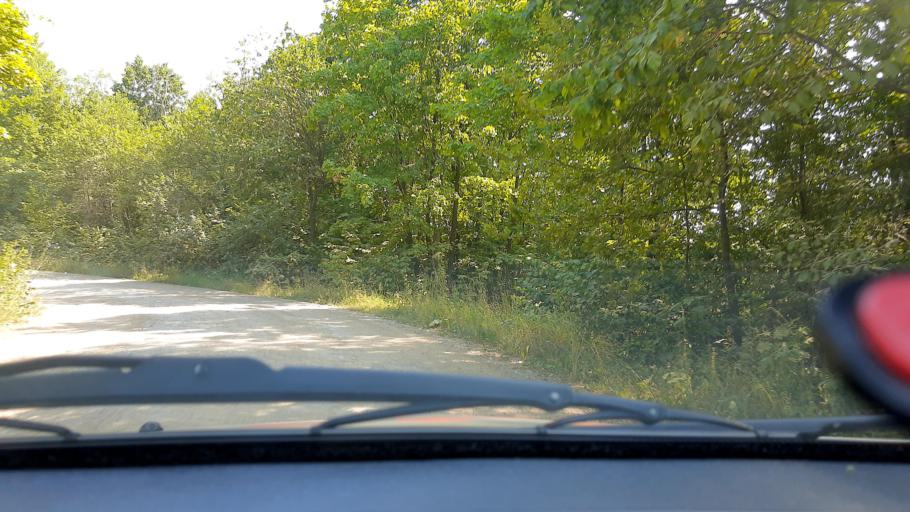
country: RU
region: Bashkortostan
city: Karmaskaly
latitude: 54.3866
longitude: 55.9089
